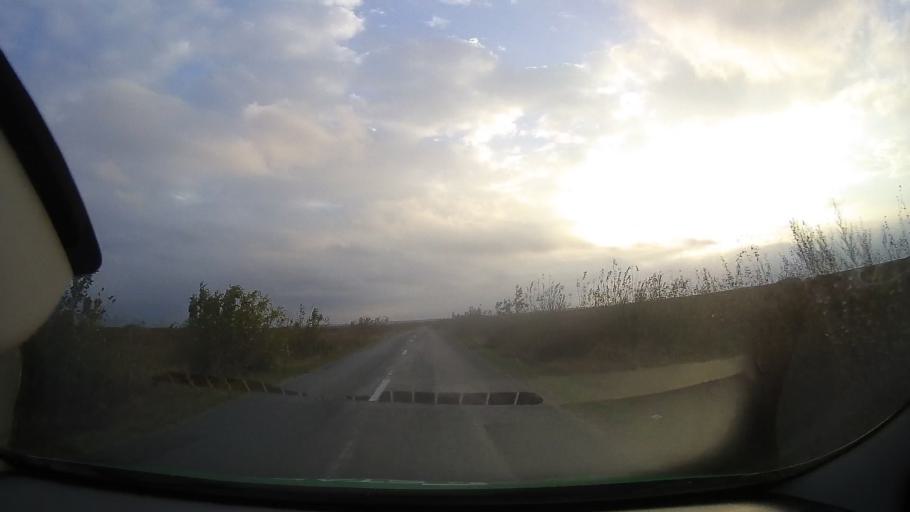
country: RO
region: Constanta
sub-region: Comuna Adamclisi
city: Adamclisi
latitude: 44.0218
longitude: 27.9072
